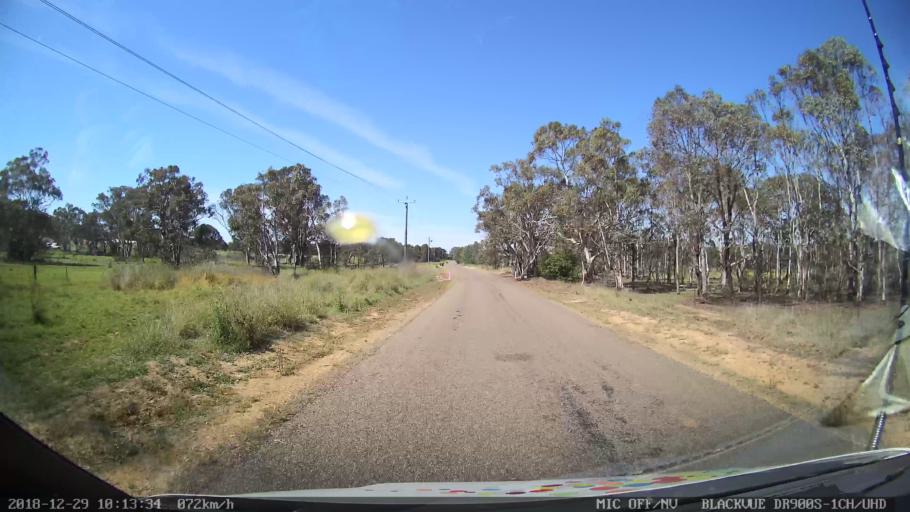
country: AU
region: New South Wales
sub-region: Yass Valley
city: Gundaroo
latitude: -34.9045
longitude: 149.4431
